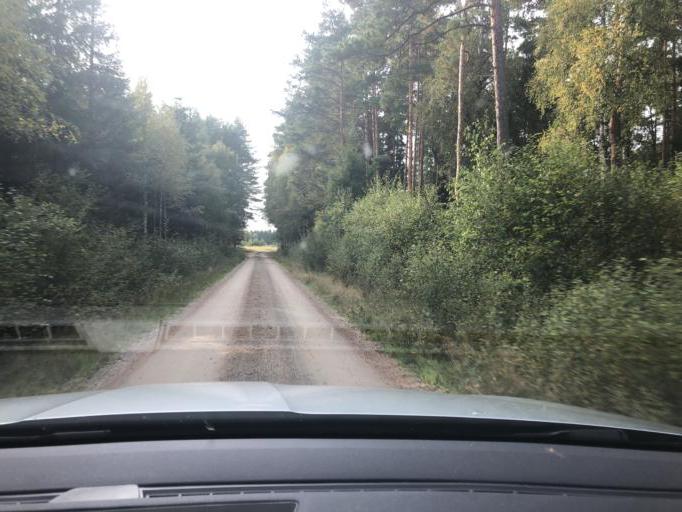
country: SE
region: Joenkoeping
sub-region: Vetlanda Kommun
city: Ekenassjon
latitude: 57.4996
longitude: 14.8985
